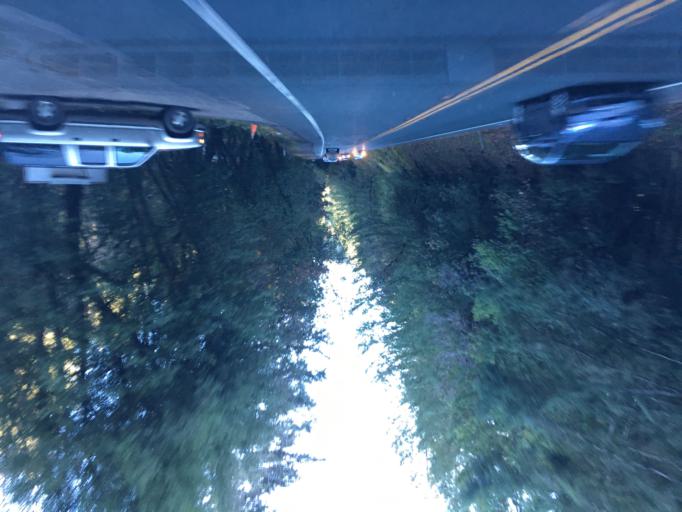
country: US
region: California
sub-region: Mendocino County
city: Brooktrails
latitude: 39.4982
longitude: -123.3711
